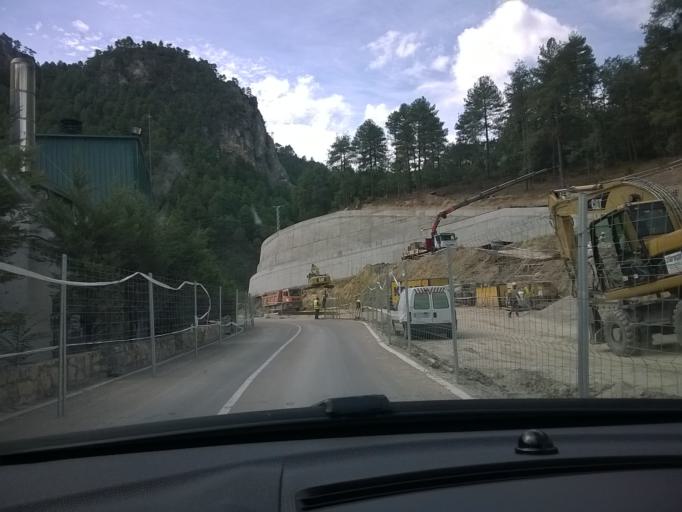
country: ES
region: Castille-La Mancha
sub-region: Provincia de Cuenca
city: Fuertescusa
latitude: 40.5085
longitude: -2.1289
